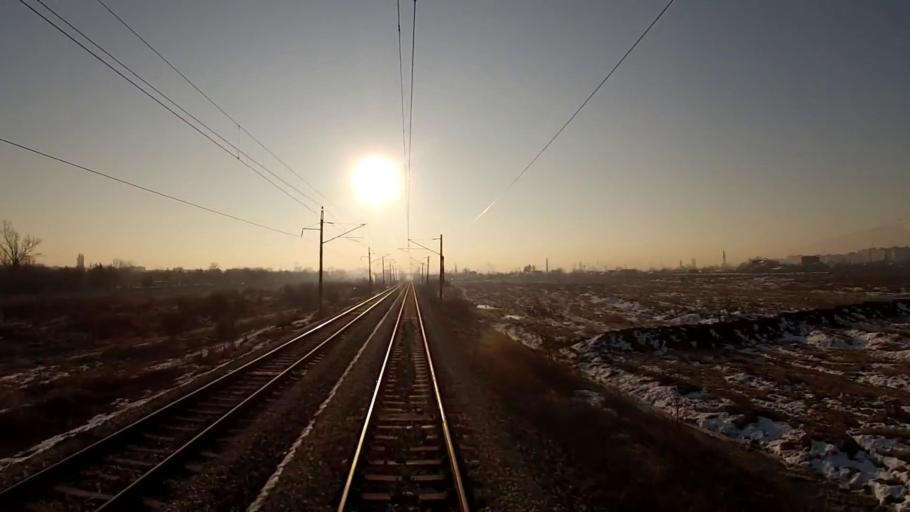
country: BG
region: Sofiya
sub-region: Obshtina Bozhurishte
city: Bozhurishte
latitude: 42.7409
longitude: 23.2612
